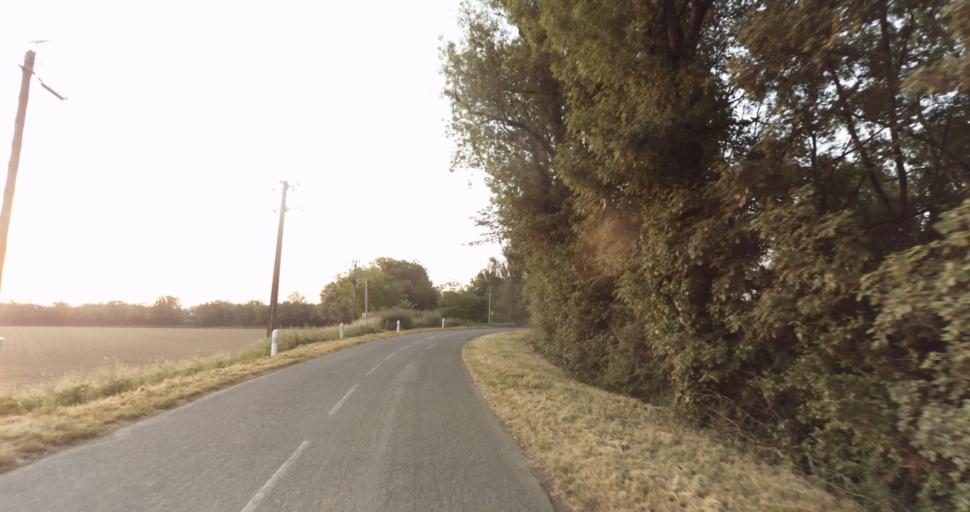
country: FR
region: Midi-Pyrenees
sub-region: Departement de la Haute-Garonne
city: Levignac
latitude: 43.6527
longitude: 1.1493
